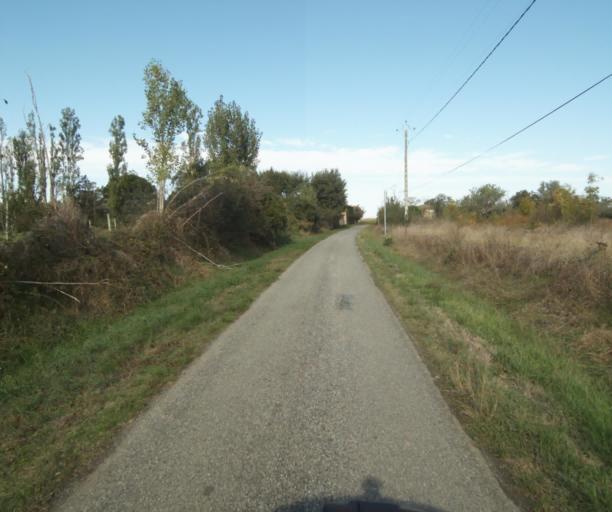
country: FR
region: Midi-Pyrenees
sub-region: Departement du Tarn-et-Garonne
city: Verdun-sur-Garonne
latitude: 43.8824
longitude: 1.2224
